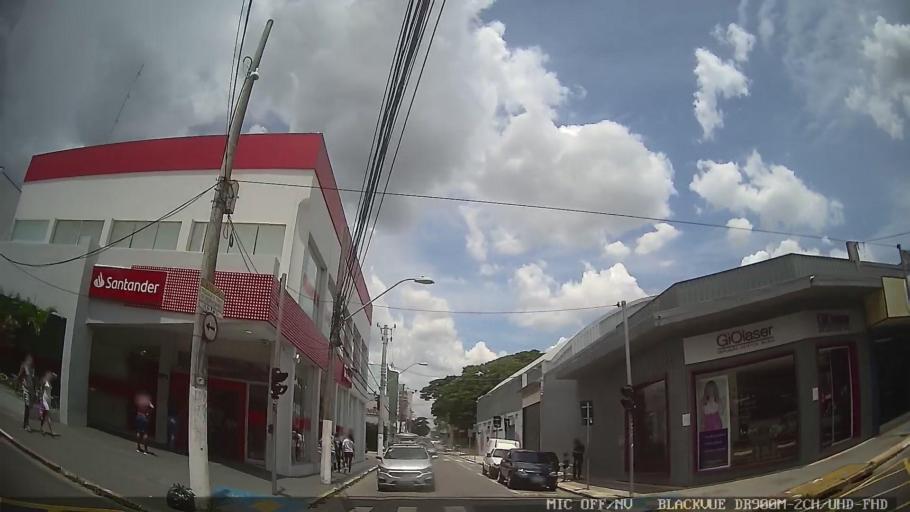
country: BR
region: Sao Paulo
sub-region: Suzano
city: Suzano
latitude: -23.5442
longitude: -46.3120
